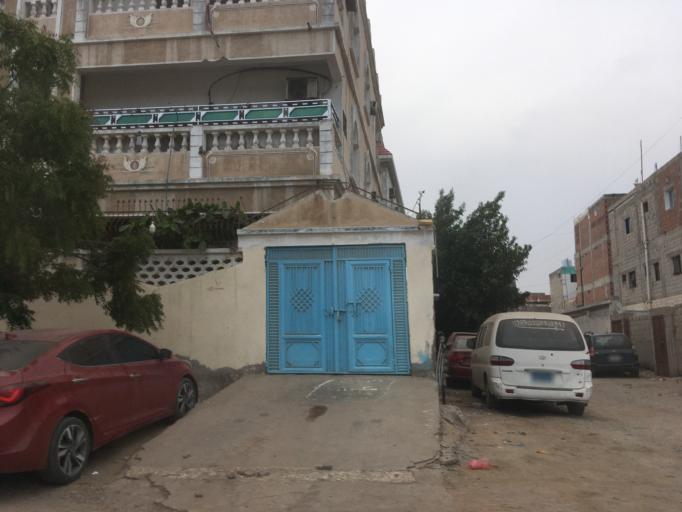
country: YE
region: Aden
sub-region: Al Mansura
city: Al Mansurah
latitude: 12.8558
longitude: 44.9897
